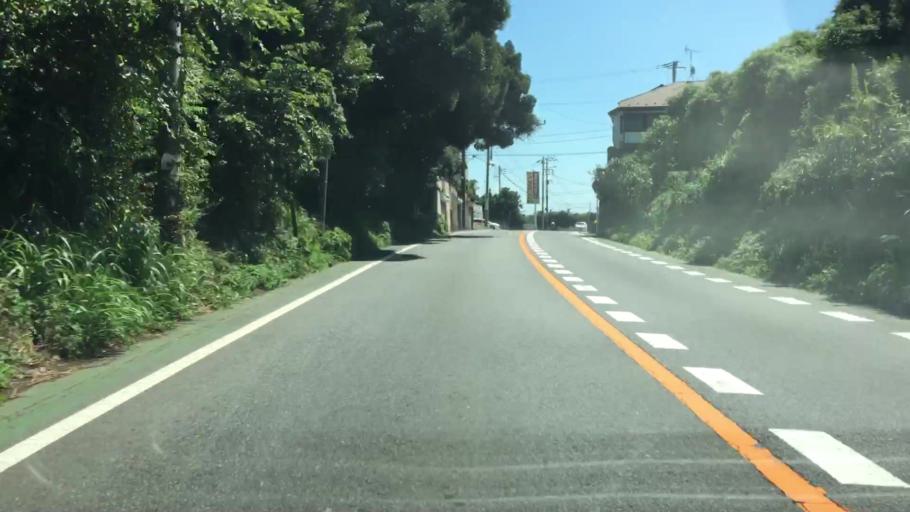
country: JP
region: Chiba
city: Funabashi
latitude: 35.7336
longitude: 139.9590
